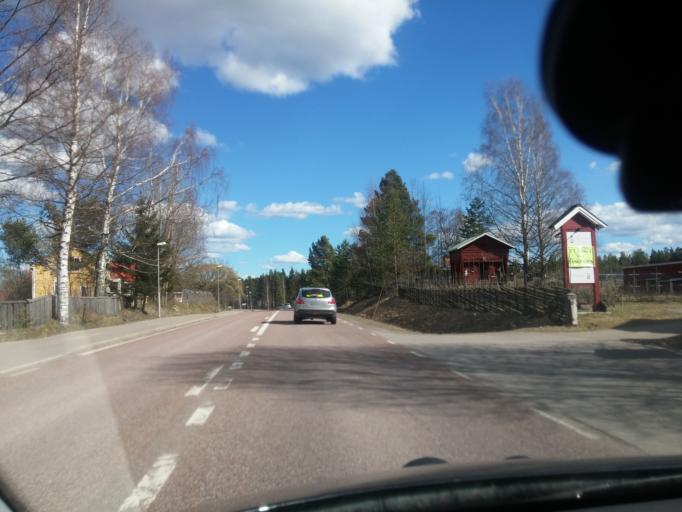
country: SE
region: Gaevleborg
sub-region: Ljusdals Kommun
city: Farila
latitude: 61.8008
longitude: 15.8839
